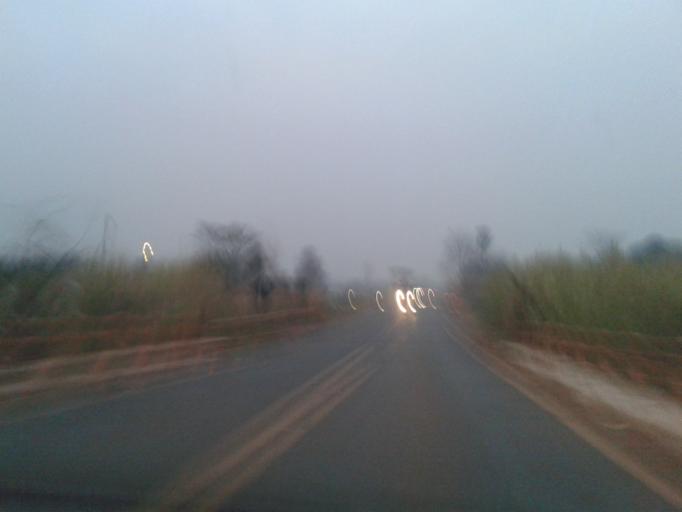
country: BR
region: Minas Gerais
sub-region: Ituiutaba
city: Ituiutaba
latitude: -18.9585
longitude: -49.4707
